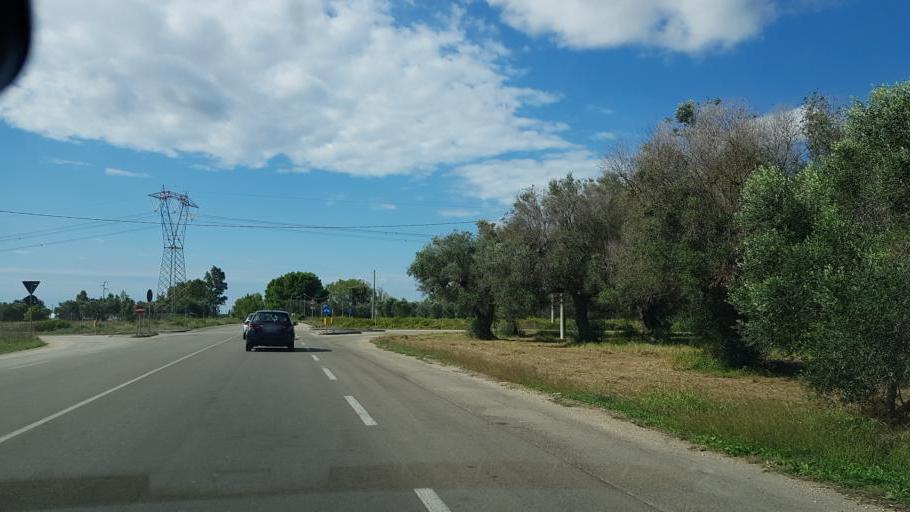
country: IT
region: Apulia
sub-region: Provincia di Lecce
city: Leverano
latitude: 40.3092
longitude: 18.0196
